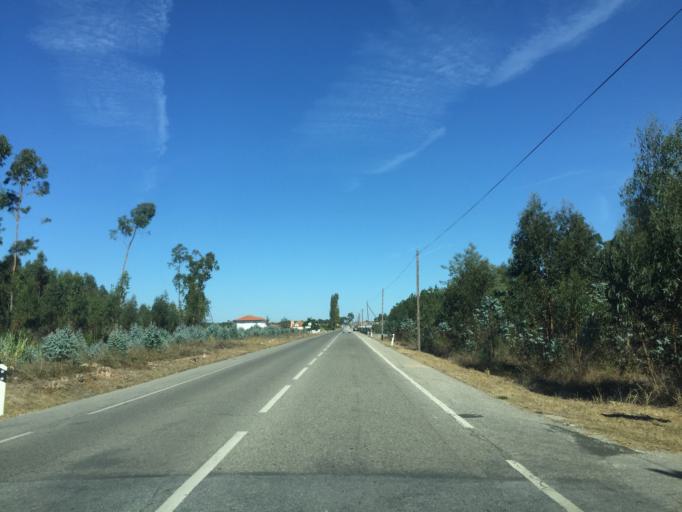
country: PT
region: Coimbra
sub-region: Figueira da Foz
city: Alhadas
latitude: 40.2474
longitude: -8.7872
